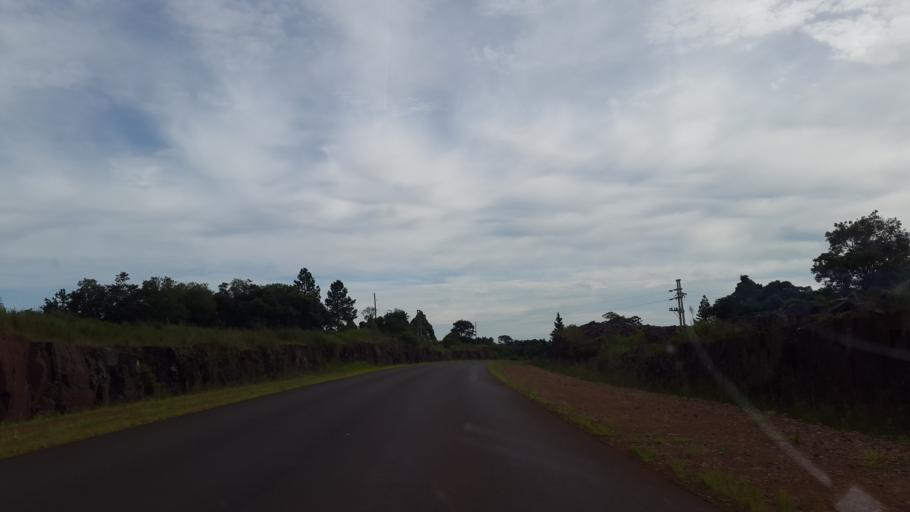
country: AR
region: Misiones
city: Bernardo de Irigoyen
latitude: -26.4306
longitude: -53.8518
